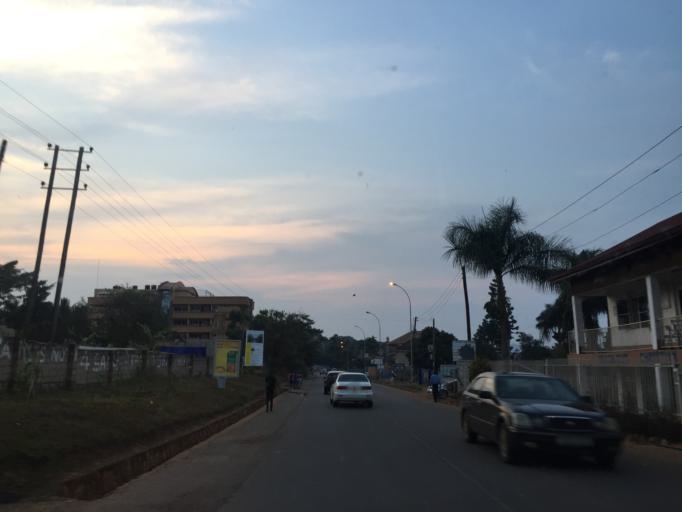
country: UG
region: Central Region
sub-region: Kampala District
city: Kampala
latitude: 0.2464
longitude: 32.6277
